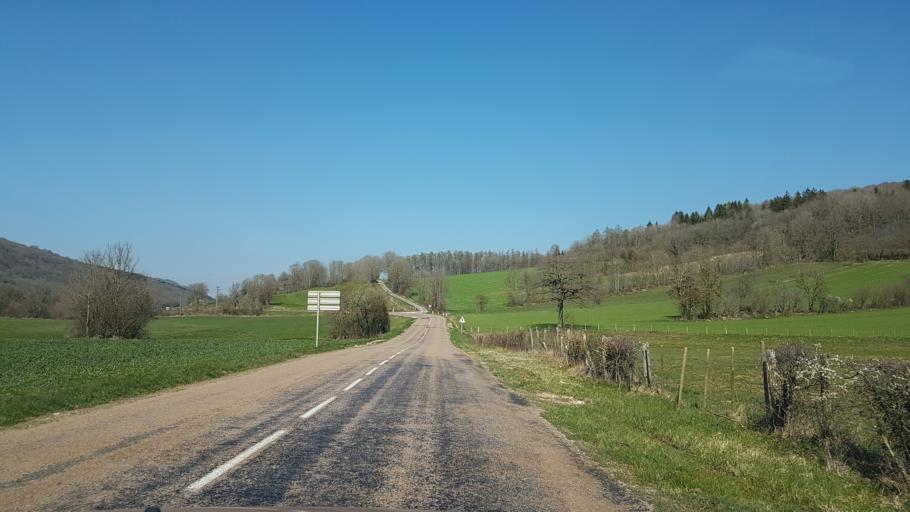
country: FR
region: Franche-Comte
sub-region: Departement du Jura
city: Orgelet
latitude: 46.5442
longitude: 5.6541
